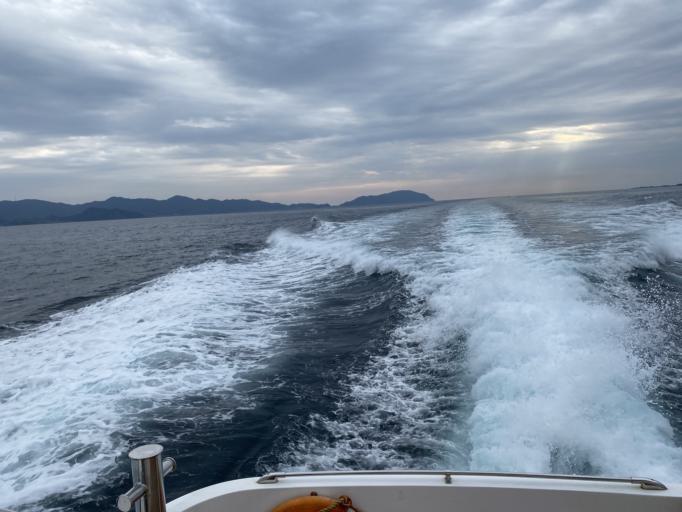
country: JP
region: Nagasaki
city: Nagasaki-shi
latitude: 32.6552
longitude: 129.7719
